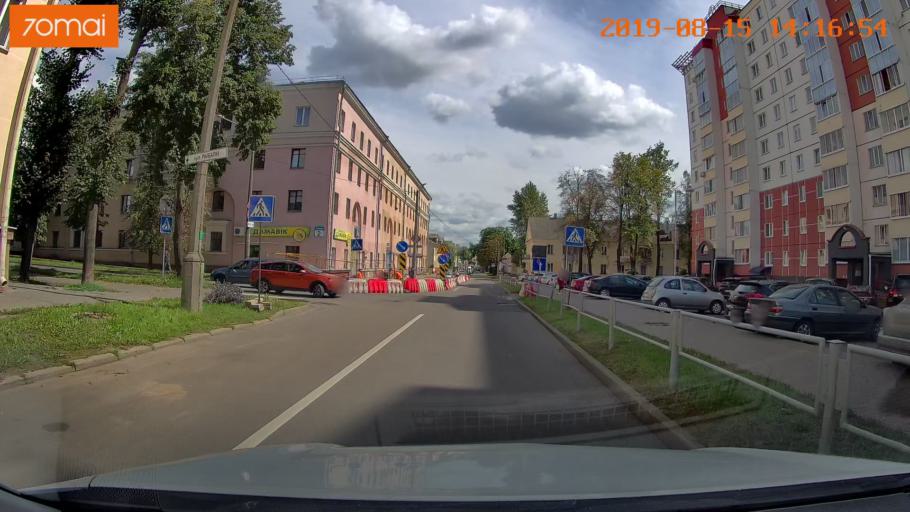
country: BY
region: Minsk
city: Minsk
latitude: 53.8849
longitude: 27.5938
